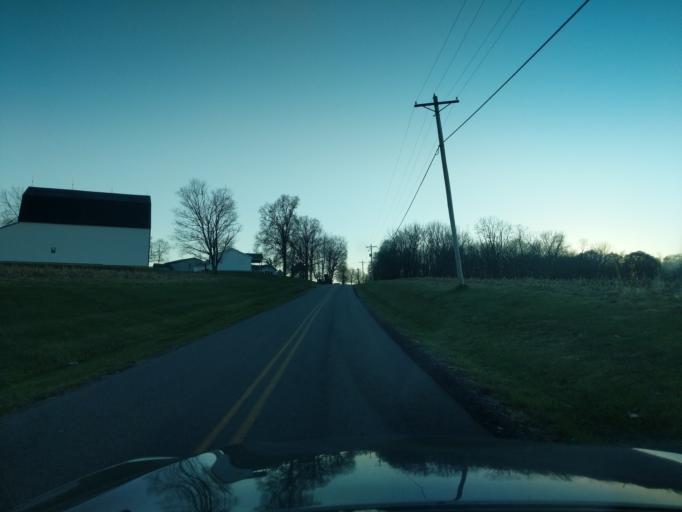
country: US
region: Ohio
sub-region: Perry County
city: Somerset
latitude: 39.8183
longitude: -82.3823
